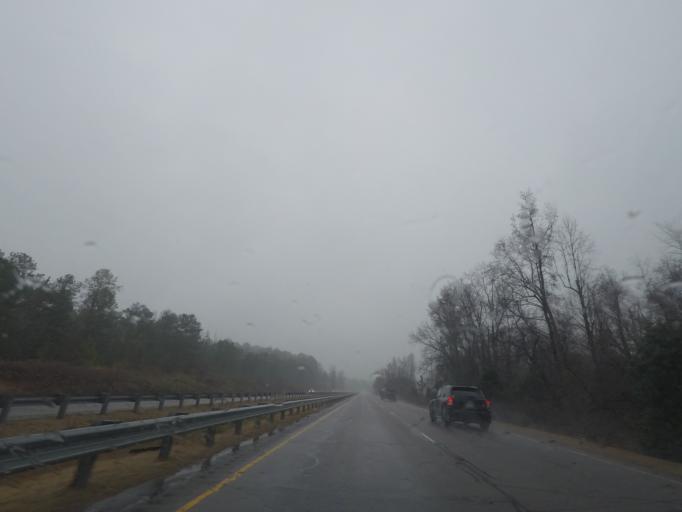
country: US
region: North Carolina
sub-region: Moore County
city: Southern Pines
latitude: 35.1855
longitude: -79.3931
